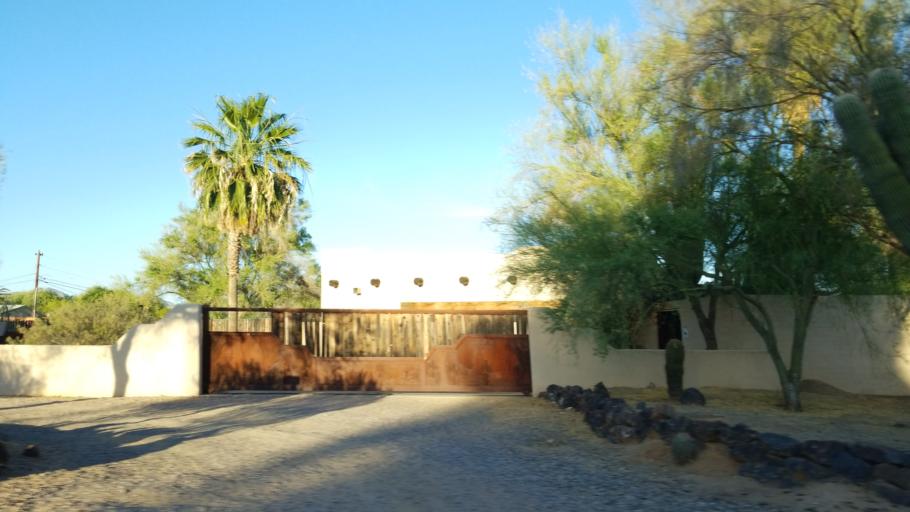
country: US
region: Arizona
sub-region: Maricopa County
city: Paradise Valley
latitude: 33.5882
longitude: -111.9086
